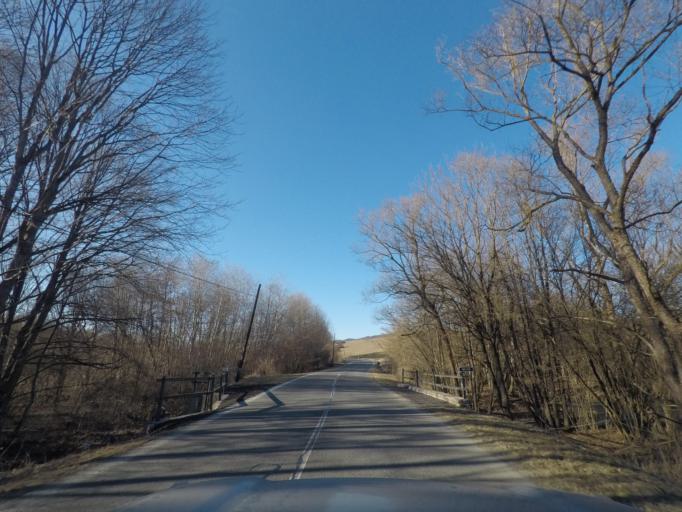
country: SK
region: Presovsky
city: Medzilaborce
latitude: 49.1830
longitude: 22.0141
